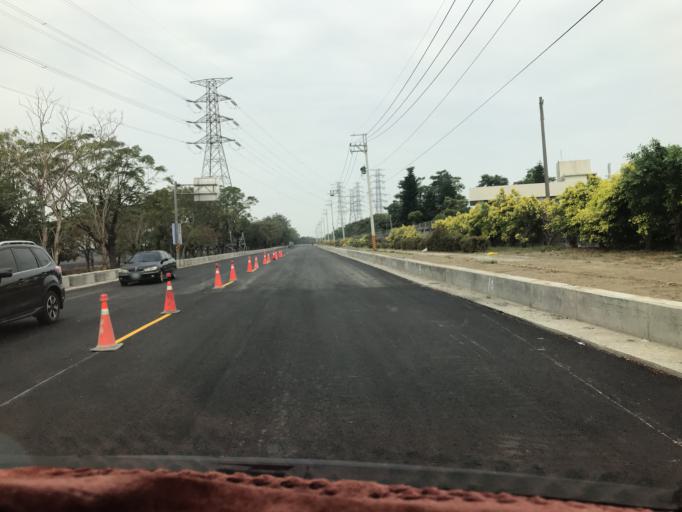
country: TW
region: Taiwan
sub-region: Pingtung
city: Pingtung
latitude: 22.4156
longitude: 120.6087
